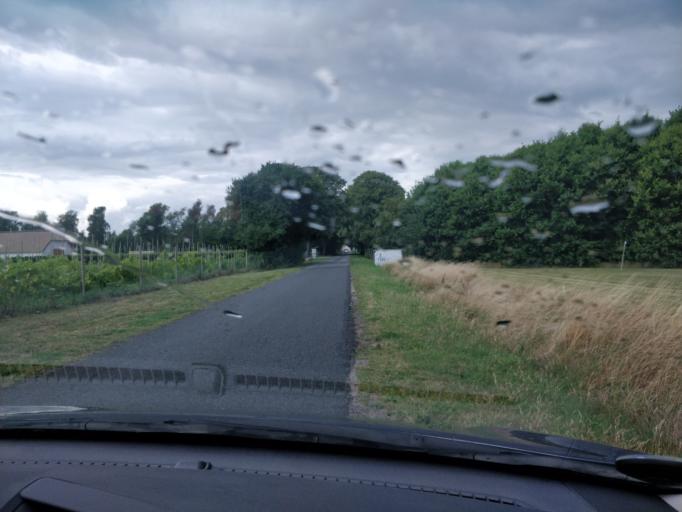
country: DK
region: South Denmark
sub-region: Assens Kommune
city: Assens
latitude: 55.2560
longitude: 9.7416
